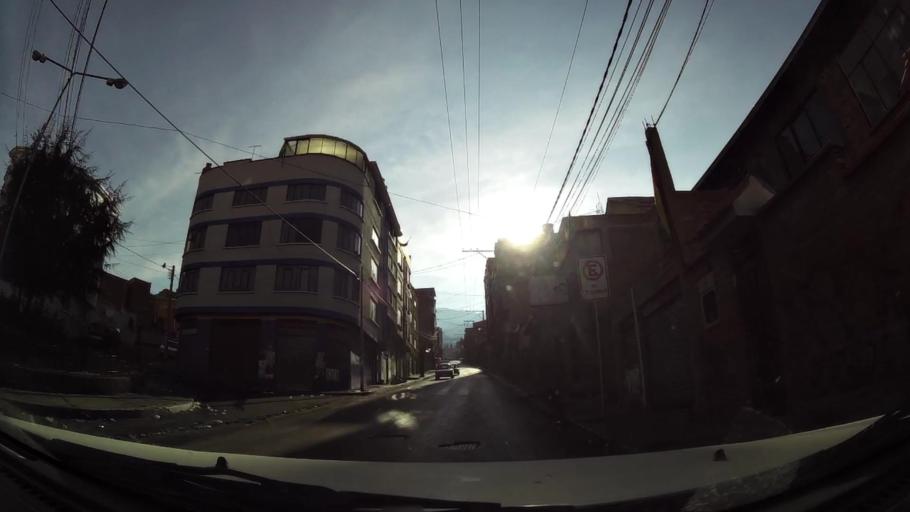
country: BO
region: La Paz
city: La Paz
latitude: -16.4934
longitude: -68.1165
